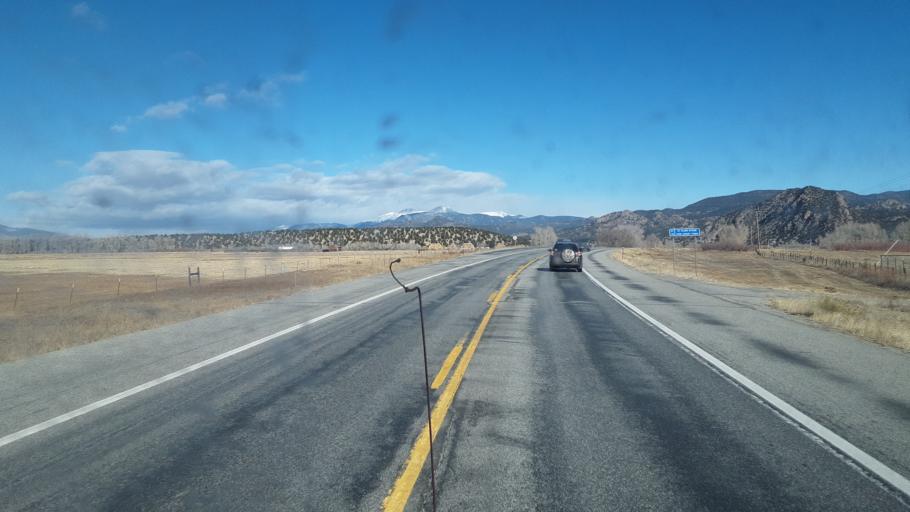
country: US
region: Colorado
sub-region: Chaffee County
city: Buena Vista
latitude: 38.7342
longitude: -106.0860
